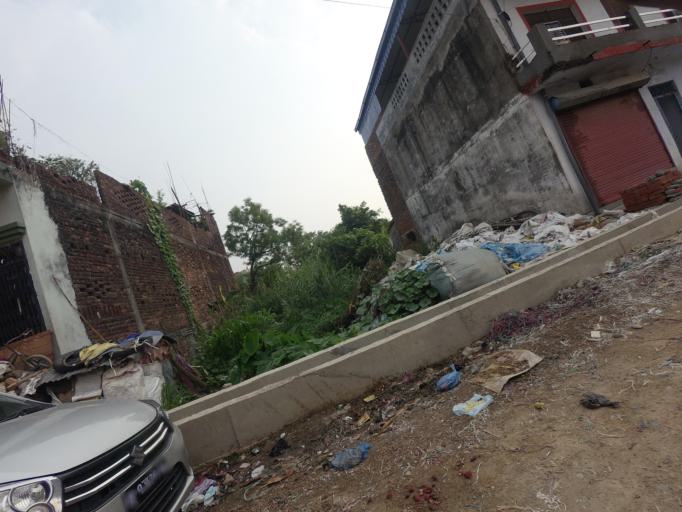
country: NP
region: Western Region
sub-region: Lumbini Zone
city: Bhairahawa
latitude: 27.5063
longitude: 83.4418
